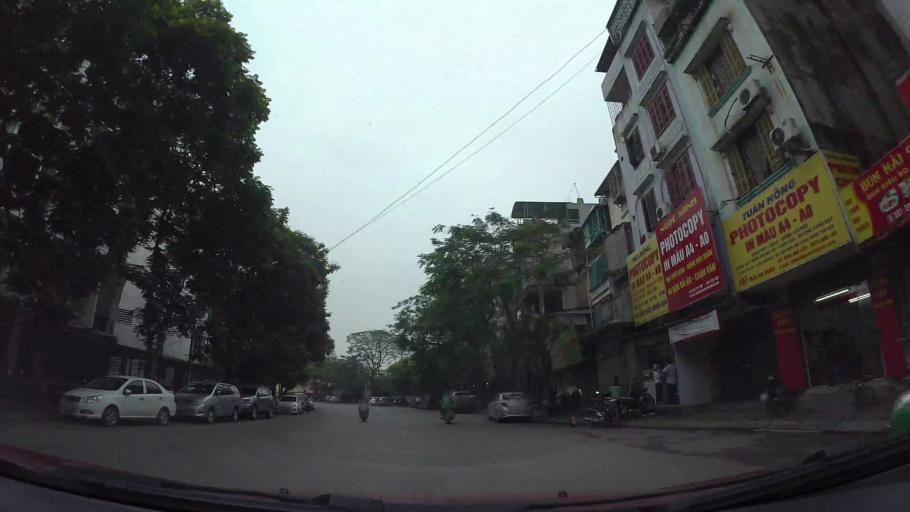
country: VN
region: Ha Noi
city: Hai BaTrung
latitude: 21.0040
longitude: 105.8452
